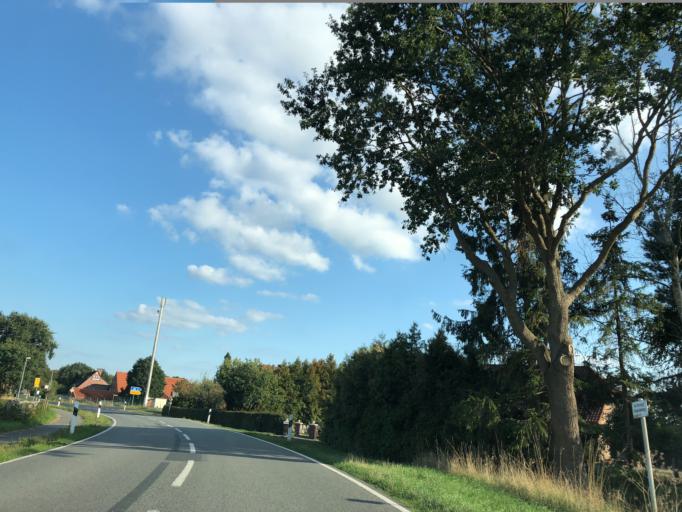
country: DE
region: Lower Saxony
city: Dersum
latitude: 53.0057
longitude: 7.2315
